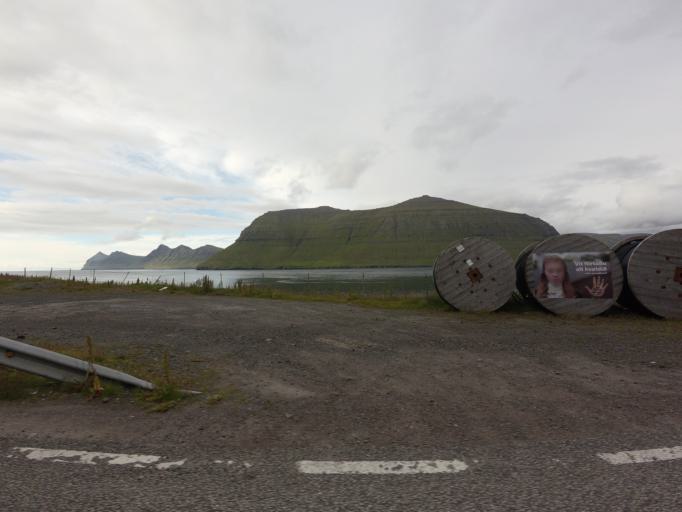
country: FO
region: Eysturoy
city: Eystur
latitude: 62.2149
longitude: -6.7181
